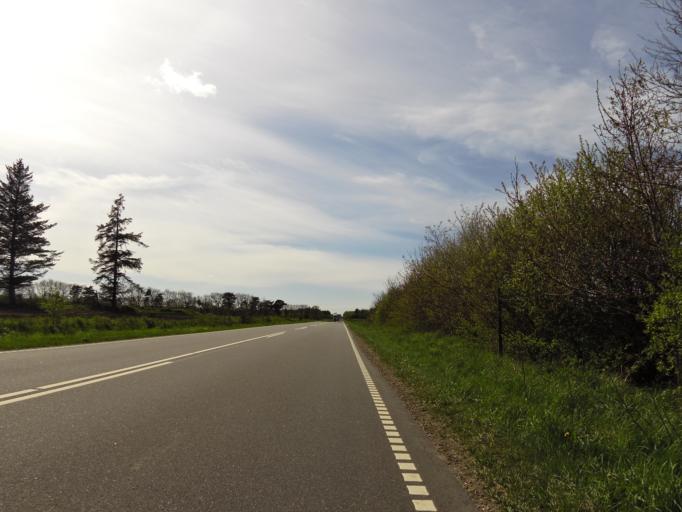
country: DK
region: Central Jutland
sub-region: Skive Kommune
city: Skive
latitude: 56.4696
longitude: 8.9418
